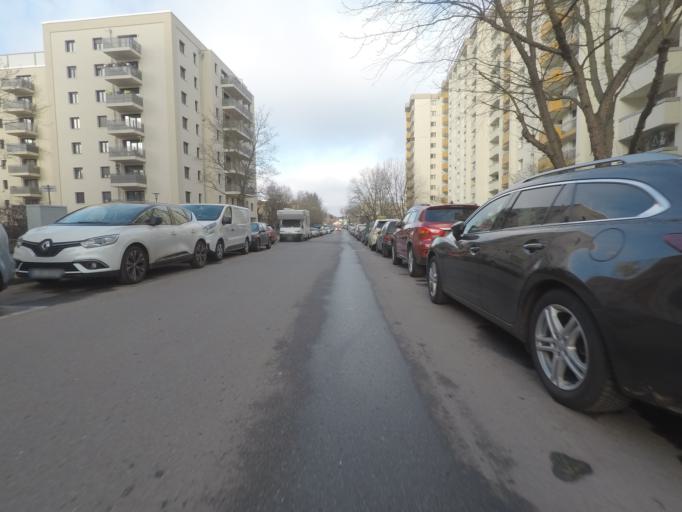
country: DE
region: Berlin
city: Marienfelde
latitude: 52.4098
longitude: 13.3474
